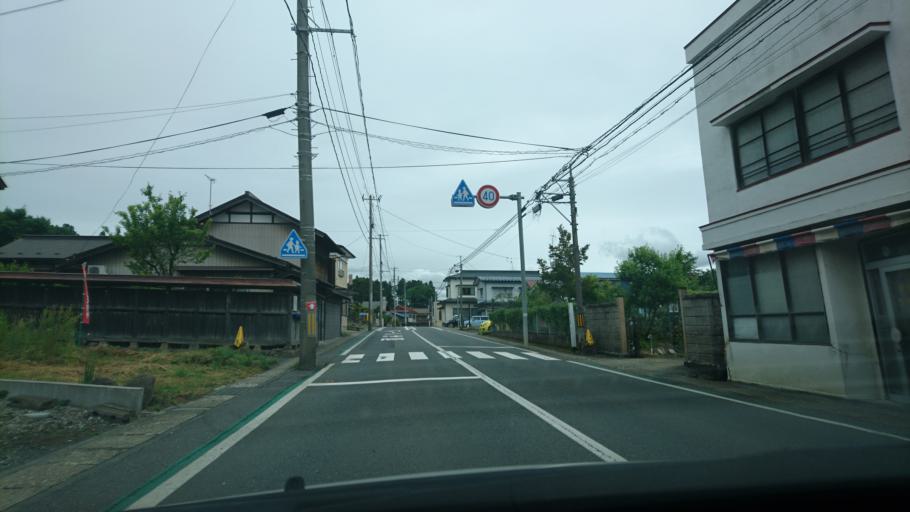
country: JP
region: Iwate
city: Ichinoseki
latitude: 38.9475
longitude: 141.1299
